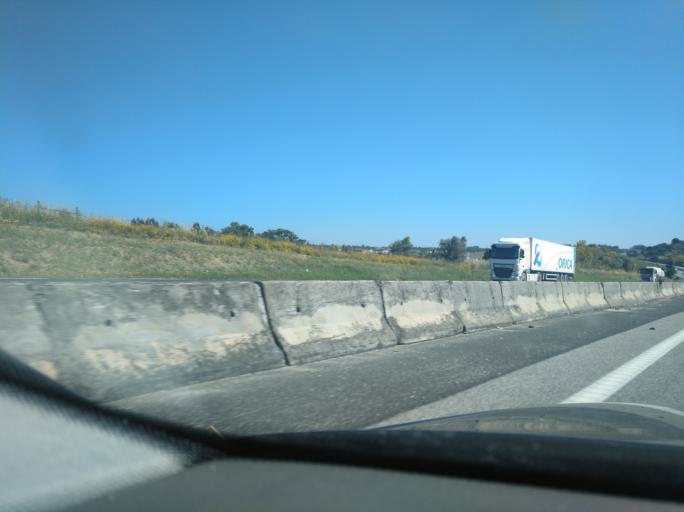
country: PT
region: Lisbon
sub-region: Azambuja
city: Aveiras de Cima
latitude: 39.1281
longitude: -8.9001
